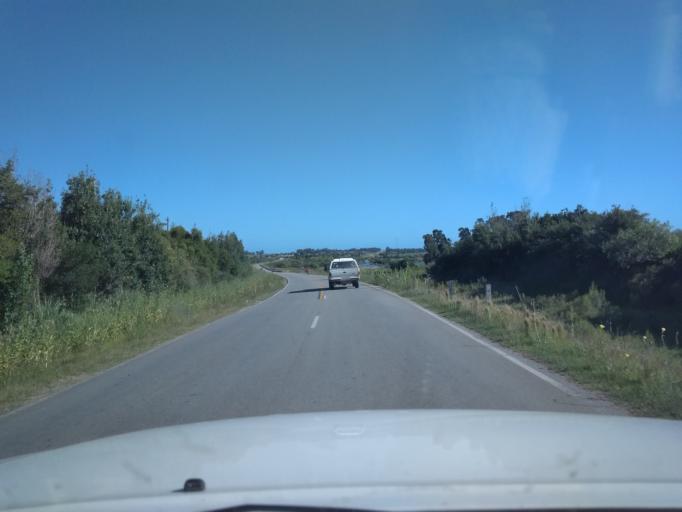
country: UY
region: Canelones
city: San Ramon
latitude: -34.3333
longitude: -55.9598
